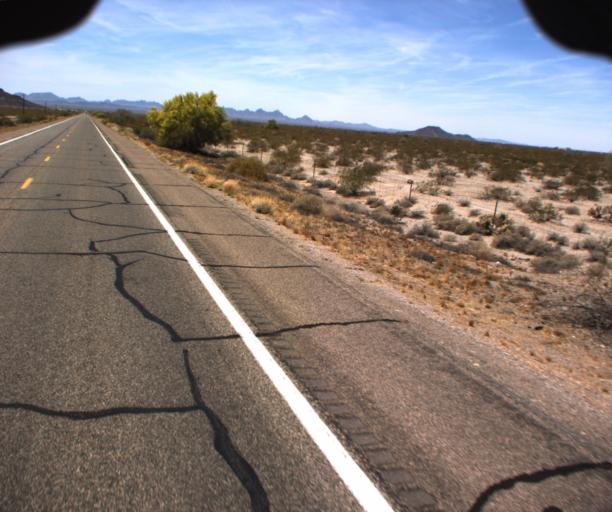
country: US
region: Arizona
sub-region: La Paz County
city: Salome
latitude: 33.7221
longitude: -113.7201
